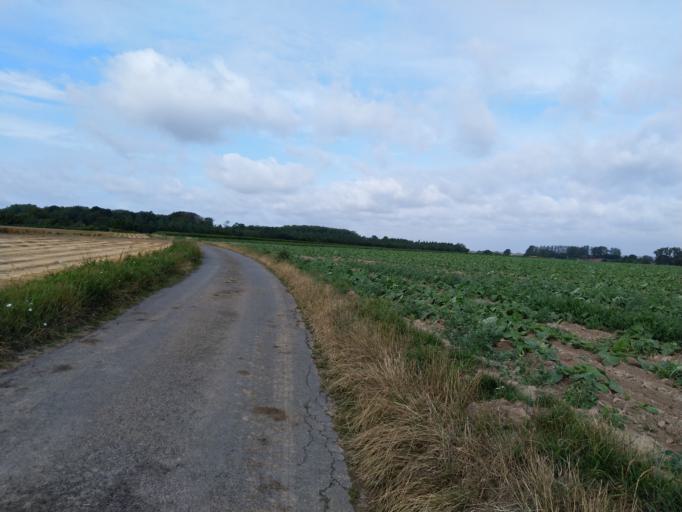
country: BE
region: Wallonia
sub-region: Province du Hainaut
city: Brugelette
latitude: 50.5541
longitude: 3.8572
